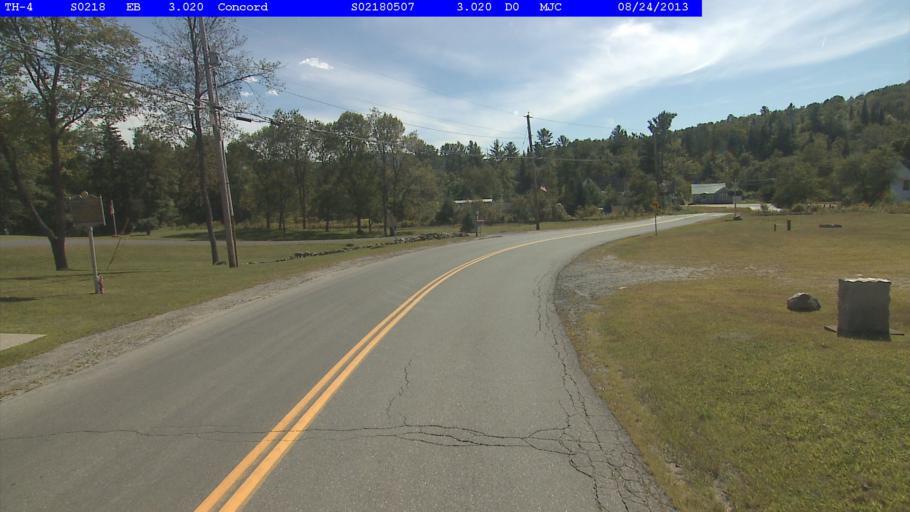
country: US
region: New Hampshire
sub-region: Grafton County
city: Littleton
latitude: 44.4256
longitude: -71.7525
